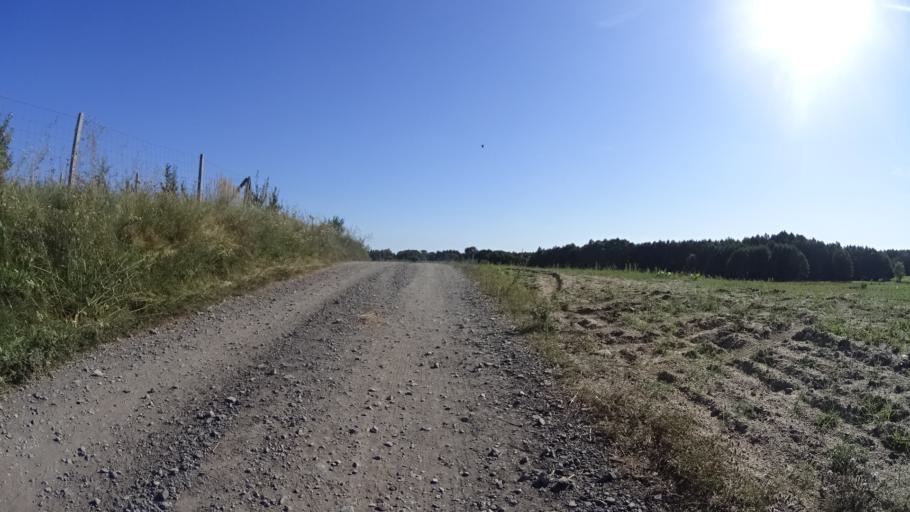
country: PL
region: Masovian Voivodeship
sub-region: Powiat bialobrzeski
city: Wysmierzyce
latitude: 51.6705
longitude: 20.8490
